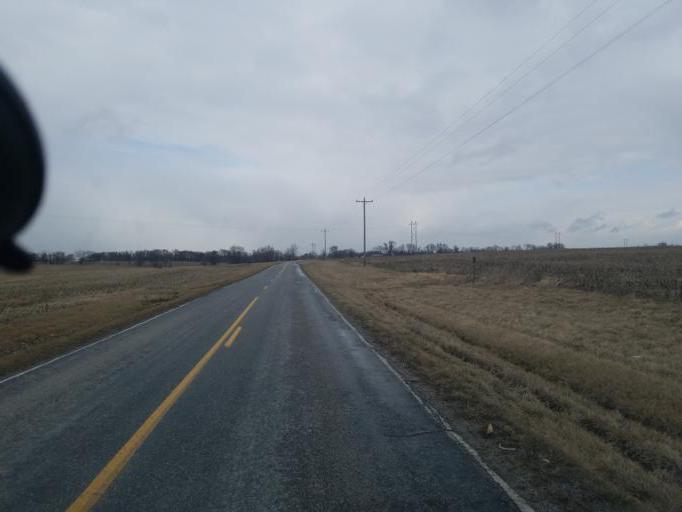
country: US
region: Missouri
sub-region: Boone County
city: Hallsville
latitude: 39.2488
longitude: -92.2927
